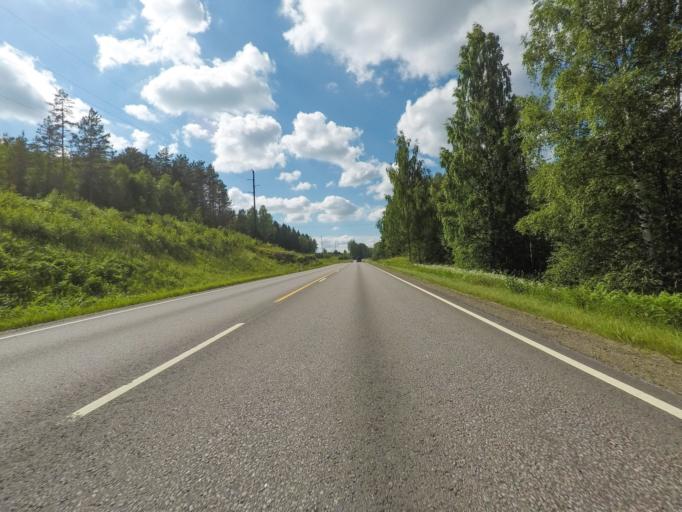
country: FI
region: Southern Savonia
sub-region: Savonlinna
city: Kerimaeki
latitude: 61.8432
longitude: 29.1989
